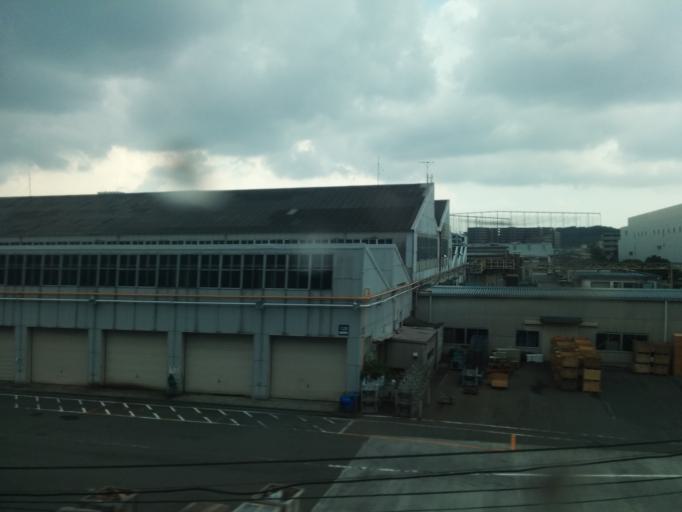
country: JP
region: Kanagawa
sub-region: Kawasaki-shi
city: Kawasaki
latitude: 35.5599
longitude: 139.6594
